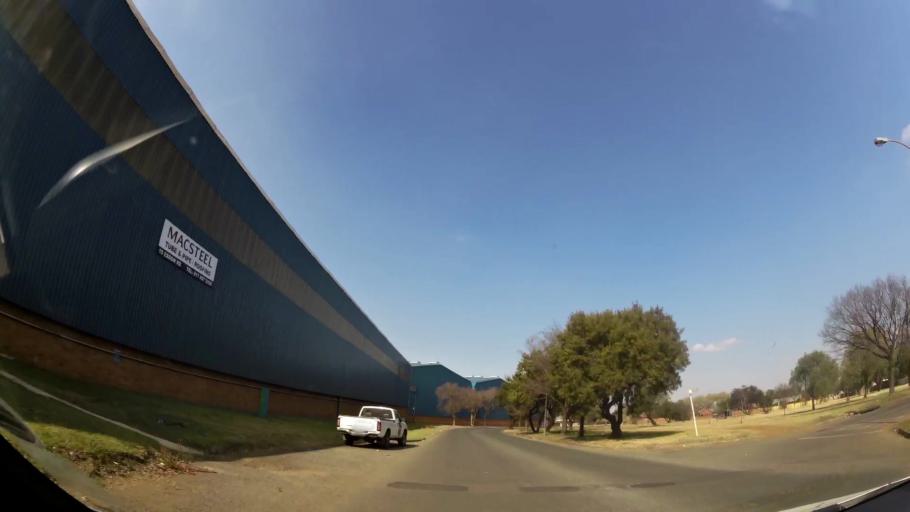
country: ZA
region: Gauteng
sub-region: Ekurhuleni Metropolitan Municipality
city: Boksburg
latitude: -26.1936
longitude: 28.2122
